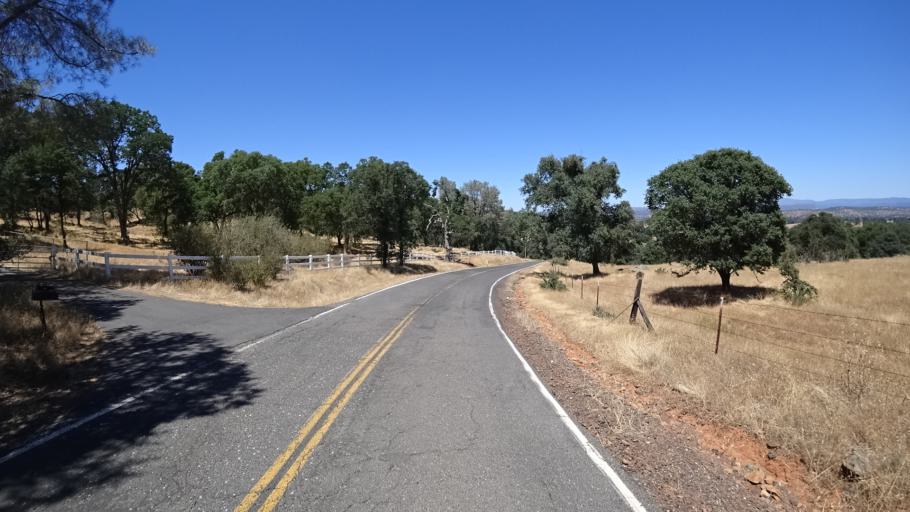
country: US
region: California
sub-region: Calaveras County
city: Copperopolis
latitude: 38.0877
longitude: -120.6627
